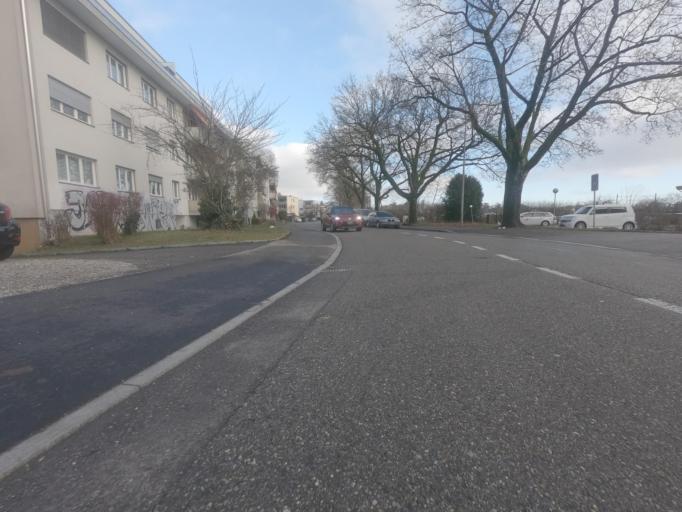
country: CH
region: Solothurn
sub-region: Bezirk Lebern
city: Langendorf
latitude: 47.2095
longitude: 7.5216
